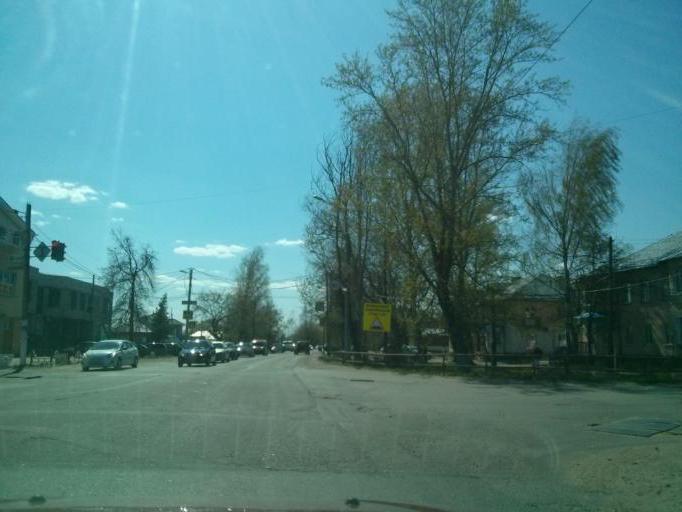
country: RU
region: Nizjnij Novgorod
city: Vorsma
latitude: 55.9881
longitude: 43.2747
